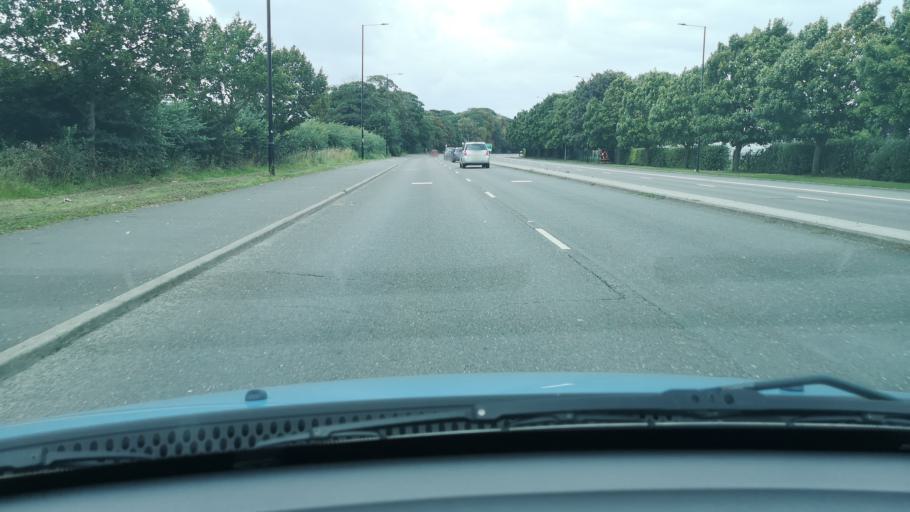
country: GB
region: England
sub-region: Doncaster
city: Bentley
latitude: 53.5436
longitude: -1.1722
